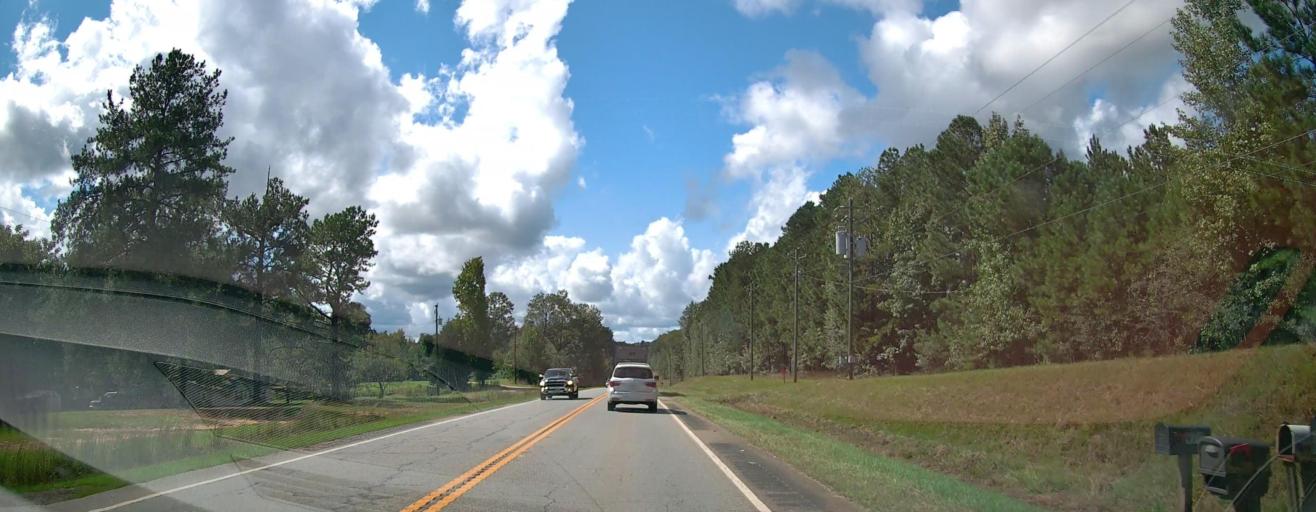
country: US
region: Georgia
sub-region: Jones County
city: Gray
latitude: 33.0277
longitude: -83.4624
